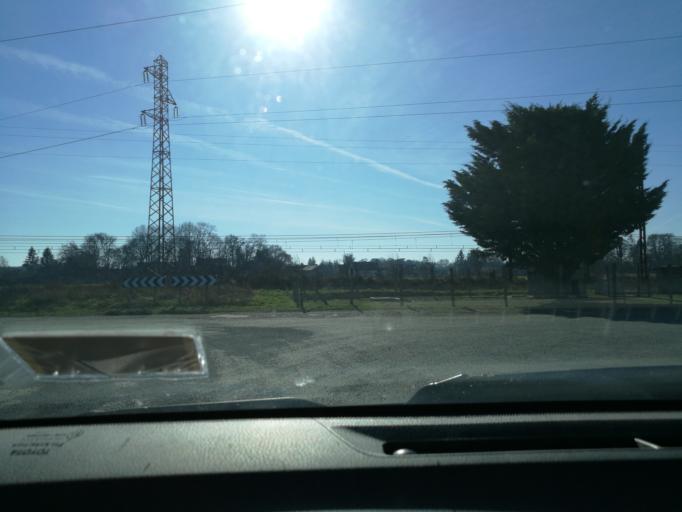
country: FR
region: Centre
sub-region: Departement du Loiret
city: Mareau-aux-Pres
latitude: 47.8794
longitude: 1.7878
